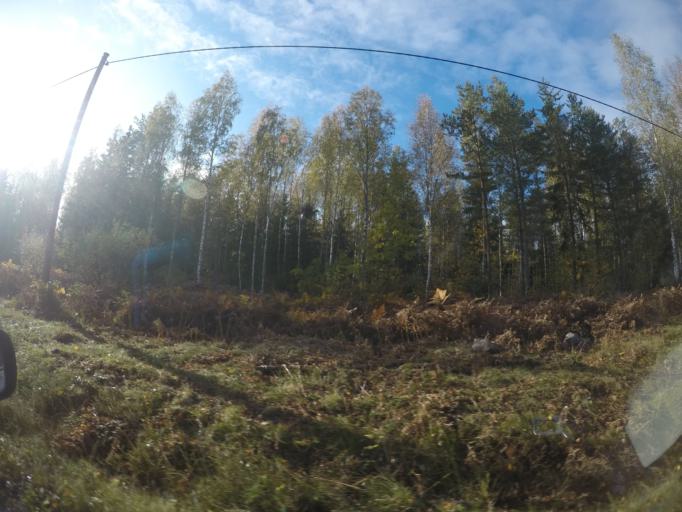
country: SE
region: Soedermanland
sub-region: Eskilstuna Kommun
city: Kvicksund
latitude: 59.3697
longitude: 16.2643
